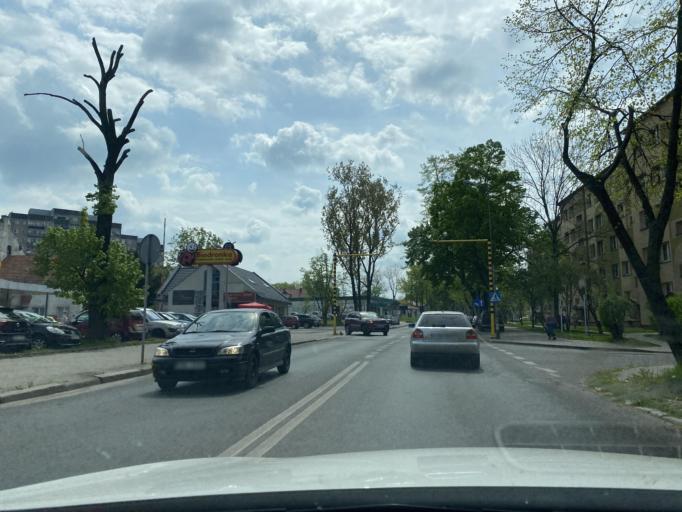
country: PL
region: Lower Silesian Voivodeship
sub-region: Powiat boleslawiecki
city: Boleslawiec
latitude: 51.2633
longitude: 15.5746
